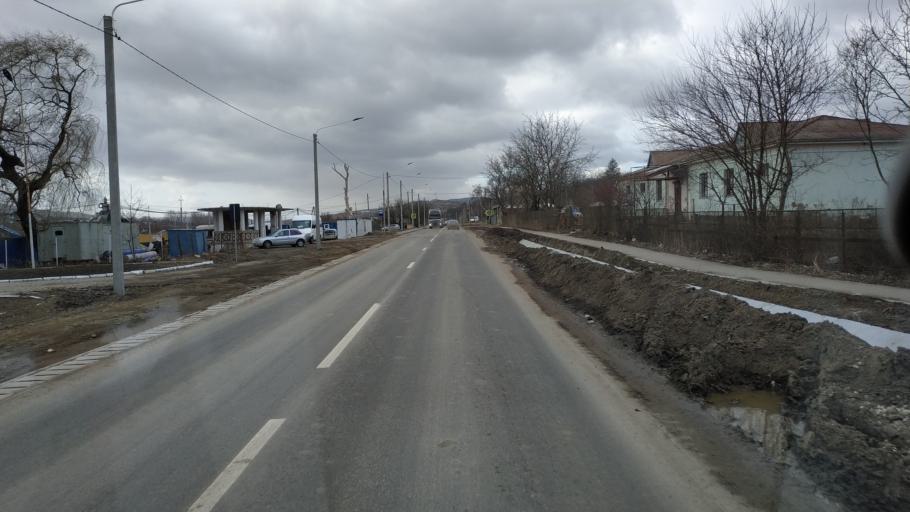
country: MD
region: Calarasi
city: Calarasi
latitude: 47.2809
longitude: 28.2081
